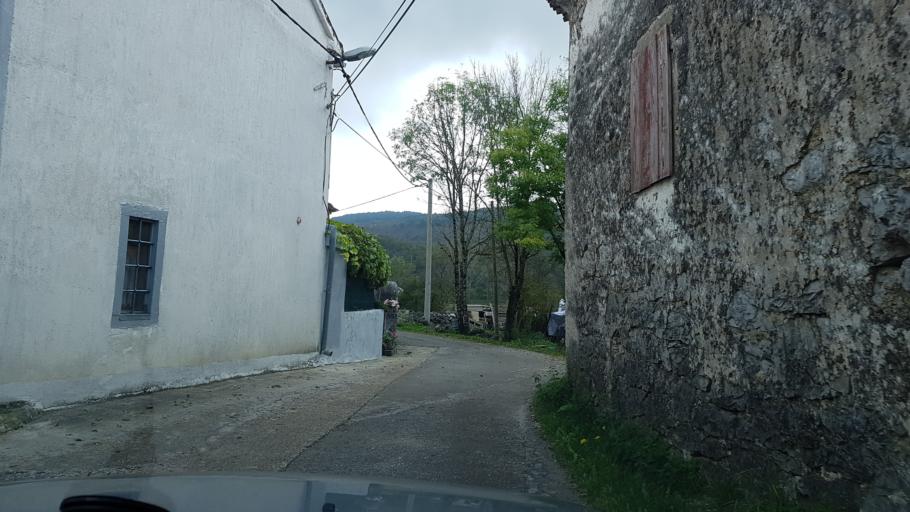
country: HR
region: Istarska
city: Buzet
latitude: 45.4106
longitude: 14.1036
